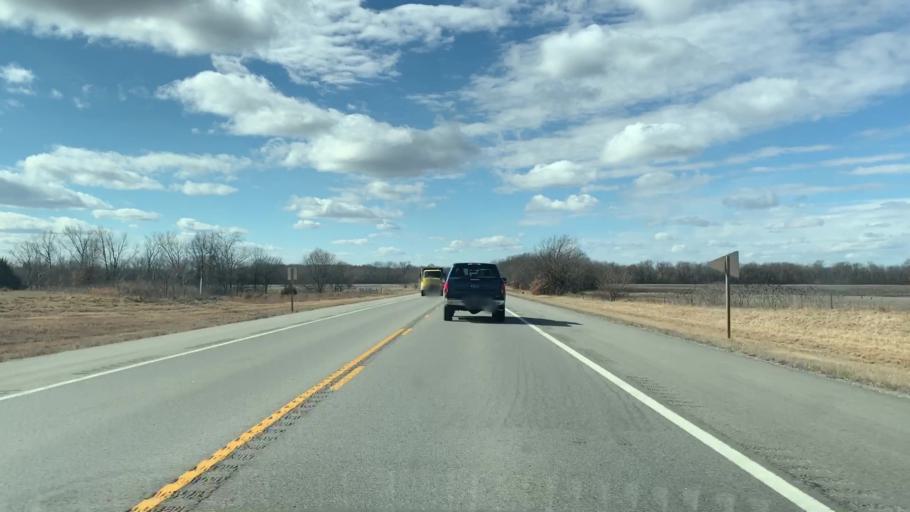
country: US
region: Kansas
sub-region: Cherokee County
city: Columbus
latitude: 37.3401
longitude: -94.9563
